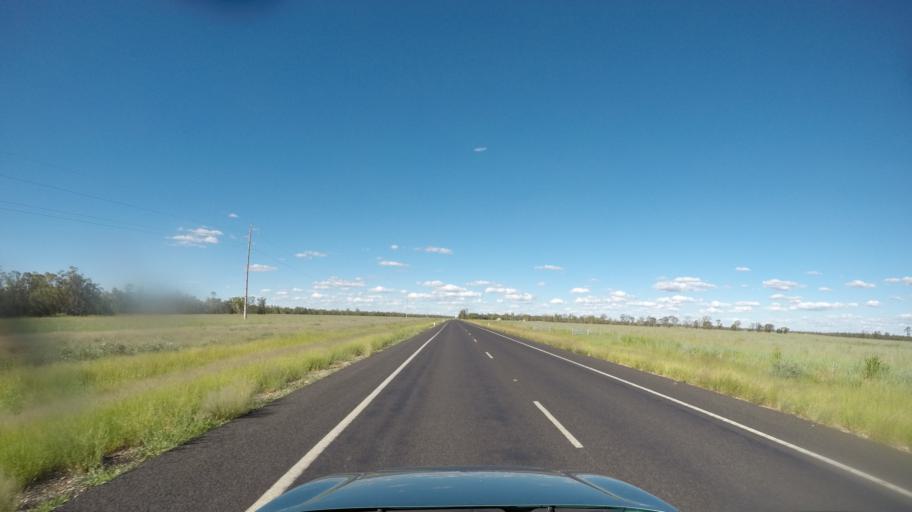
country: AU
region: Queensland
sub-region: Goondiwindi
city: Goondiwindi
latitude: -28.1248
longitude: 150.7048
